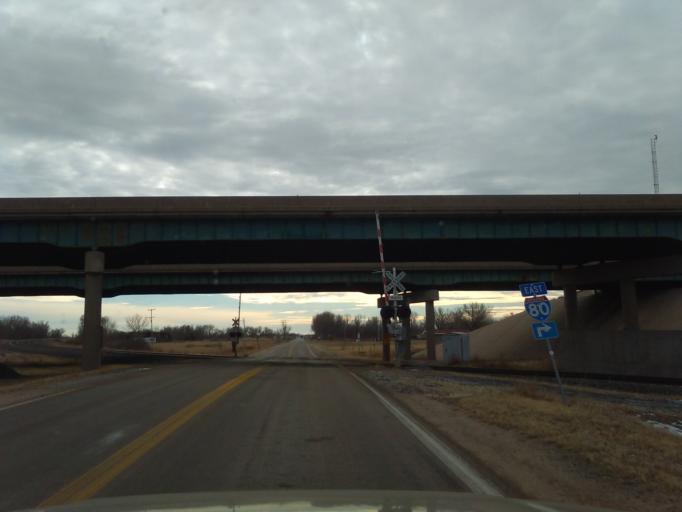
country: US
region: Nebraska
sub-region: Buffalo County
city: Shelton
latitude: 40.7232
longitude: -98.7408
